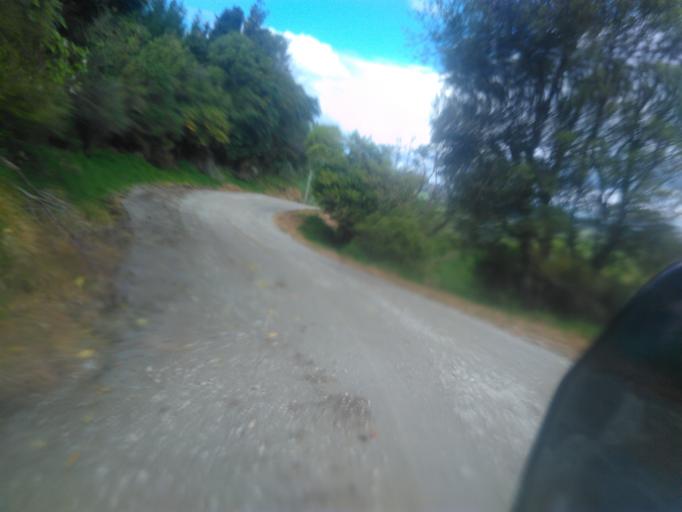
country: NZ
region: Hawke's Bay
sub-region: Wairoa District
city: Wairoa
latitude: -38.7775
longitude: 177.6287
